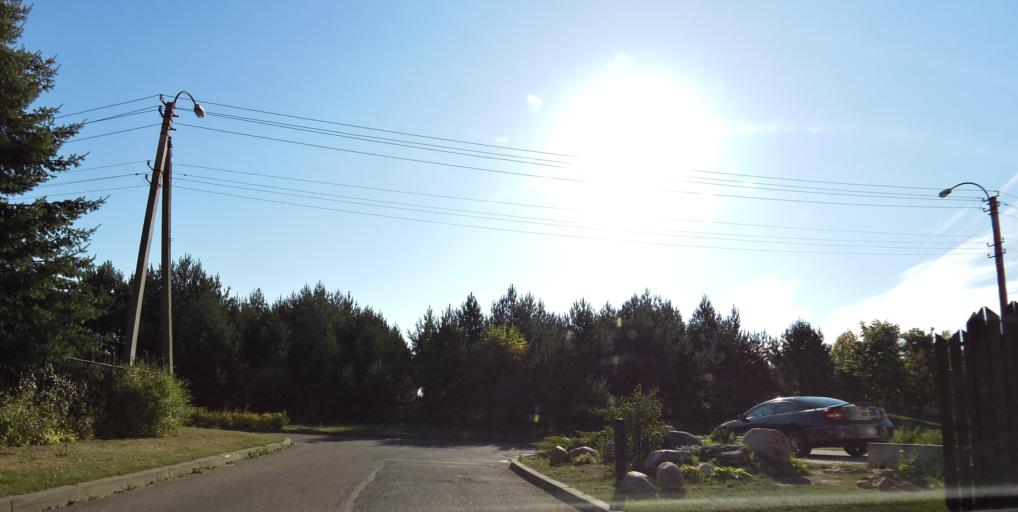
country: LT
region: Vilnius County
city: Pilaite
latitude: 54.7106
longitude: 25.1920
